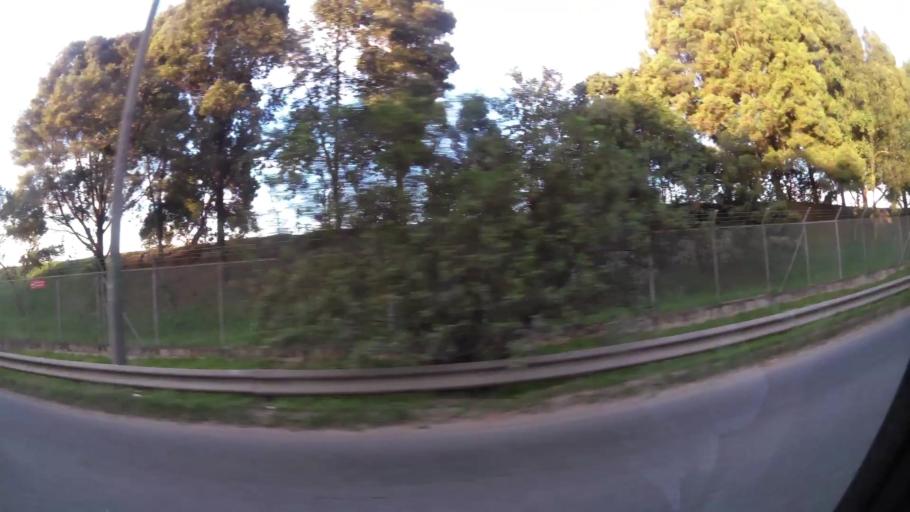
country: CO
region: Cundinamarca
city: Funza
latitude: 4.6936
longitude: -74.1496
